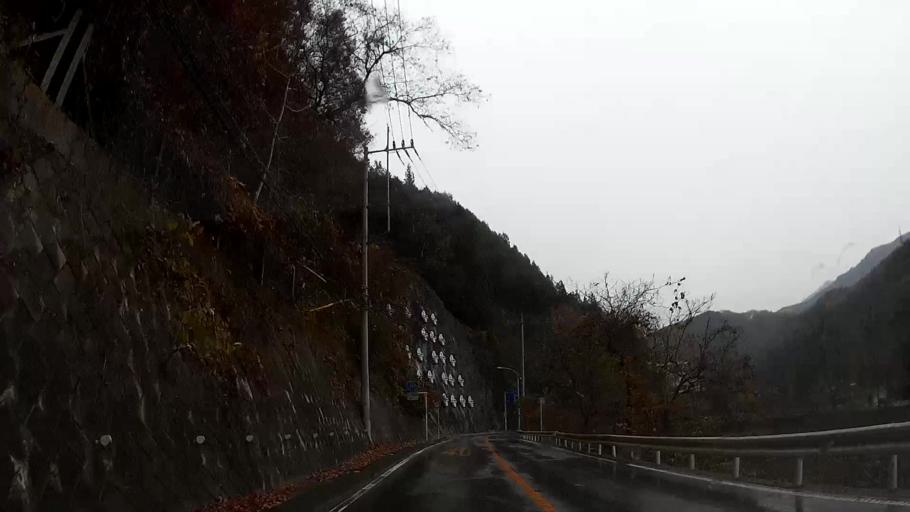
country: JP
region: Saitama
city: Chichibu
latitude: 35.9556
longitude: 138.9141
